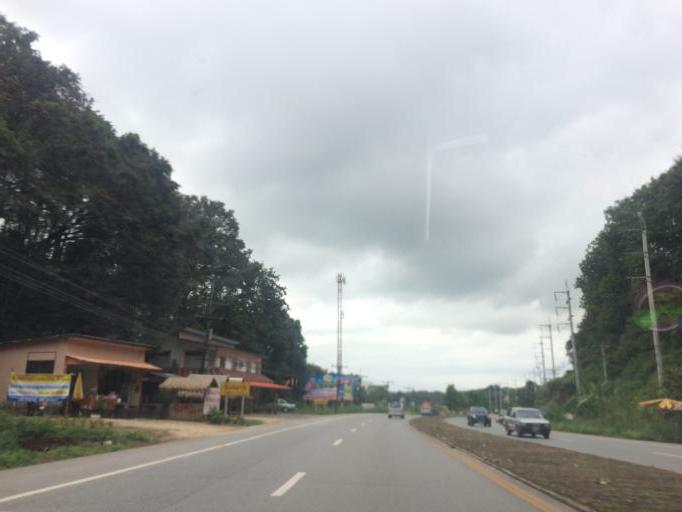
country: TH
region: Chiang Rai
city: Mae Chan
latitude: 20.1216
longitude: 99.8684
